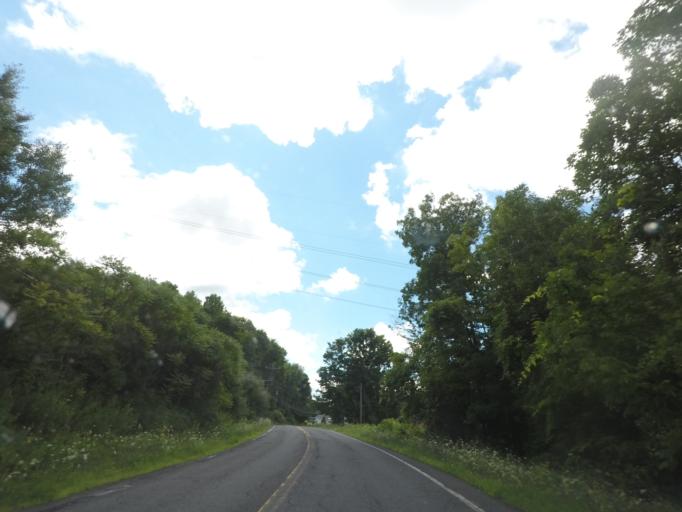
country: US
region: New York
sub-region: Rensselaer County
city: Wynantskill
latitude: 42.6681
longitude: -73.6779
